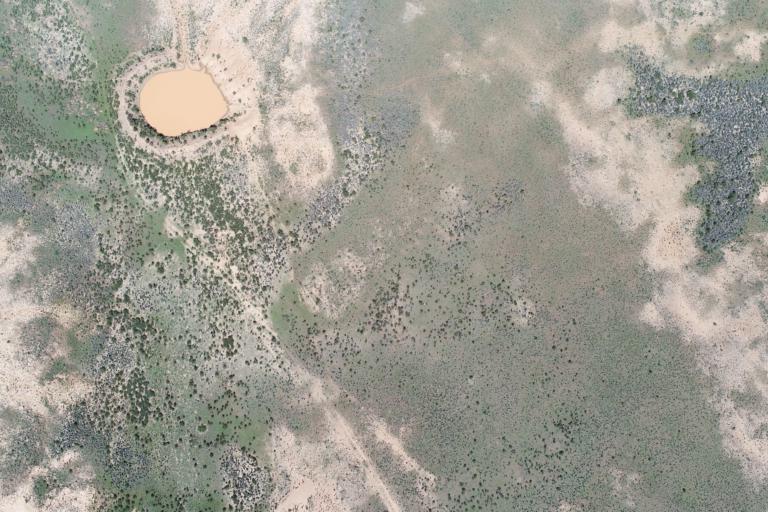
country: BO
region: La Paz
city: Curahuara de Carangas
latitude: -17.2954
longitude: -68.5205
